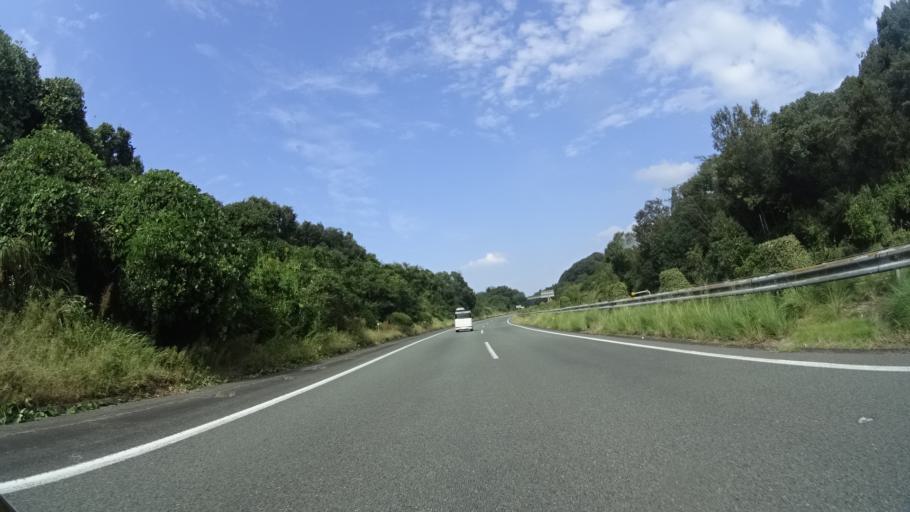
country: JP
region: Kumamoto
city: Matsubase
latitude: 32.6219
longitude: 130.7132
